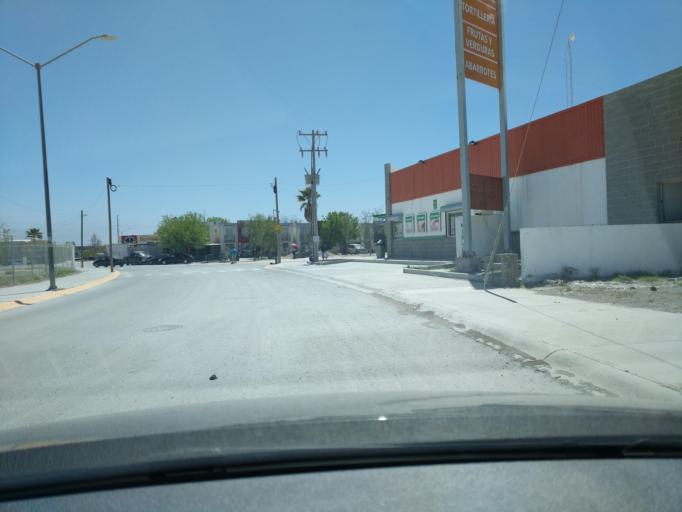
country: MX
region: Nuevo Leon
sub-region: Apodaca
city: Artemio Trevino
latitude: 25.8407
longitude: -100.1431
